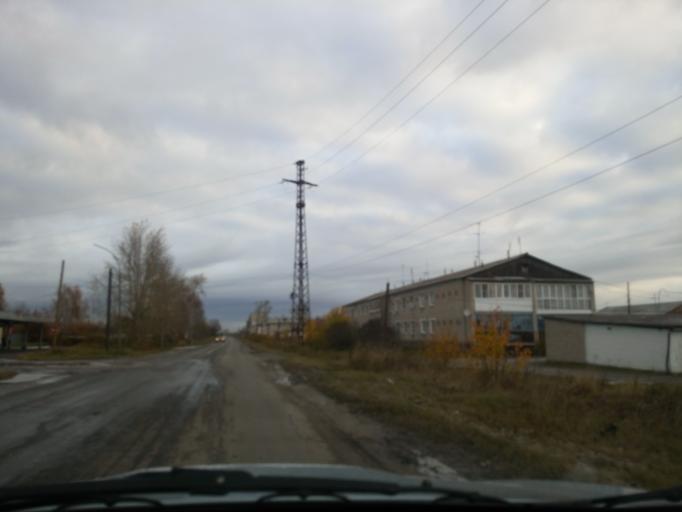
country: RU
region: Sverdlovsk
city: Turinsk
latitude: 58.0350
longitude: 63.7026
